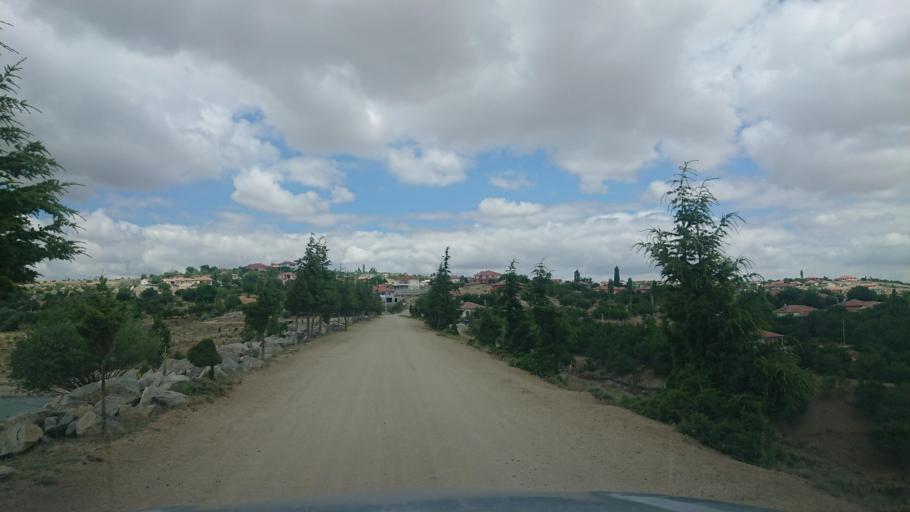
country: TR
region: Aksaray
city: Agacoren
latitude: 38.8656
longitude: 33.9501
